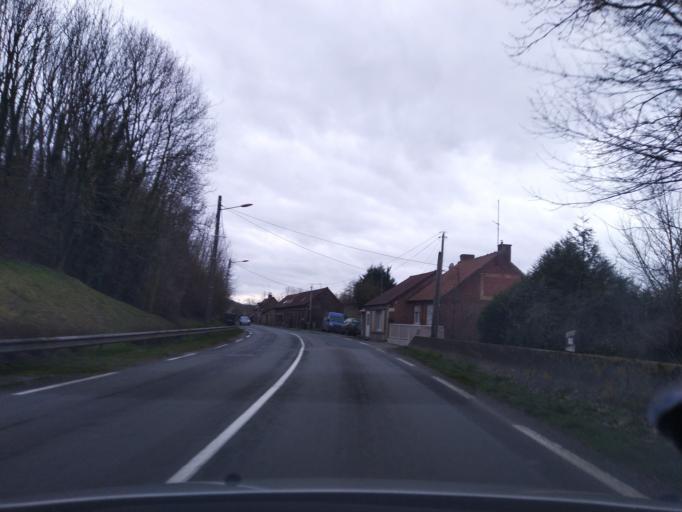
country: FR
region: Nord-Pas-de-Calais
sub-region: Departement du Pas-de-Calais
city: Divion
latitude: 50.4601
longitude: 2.4837
